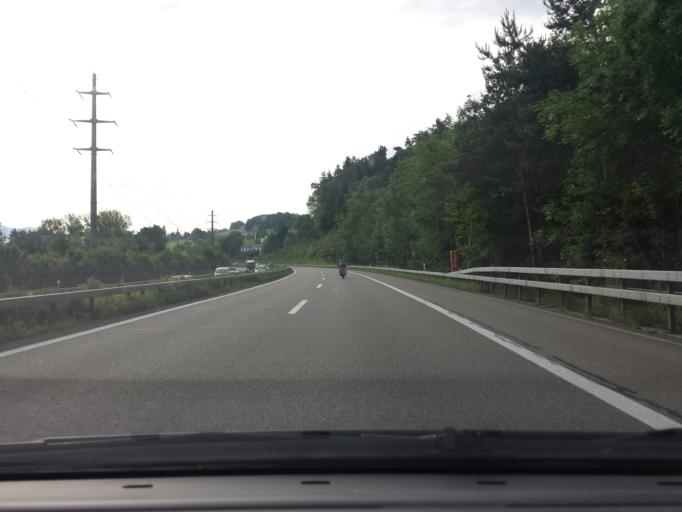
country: CH
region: Appenzell Ausserrhoden
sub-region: Bezirk Vorderland
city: Heiden
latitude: 47.4748
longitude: 9.5416
